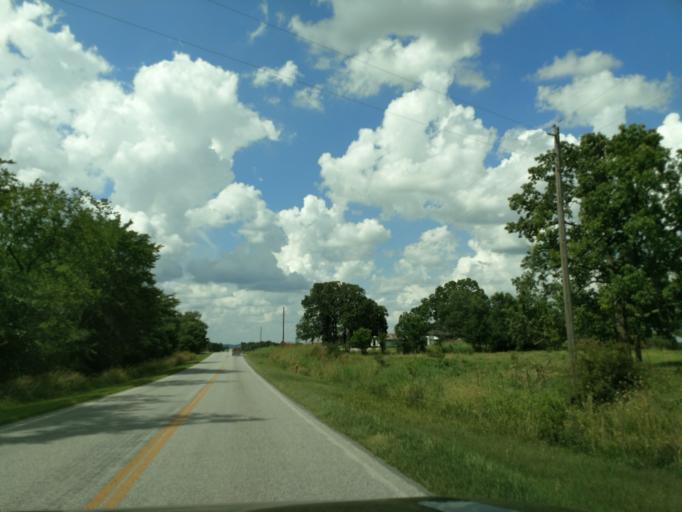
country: US
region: Arkansas
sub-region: Carroll County
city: Berryville
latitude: 36.4403
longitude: -93.5562
